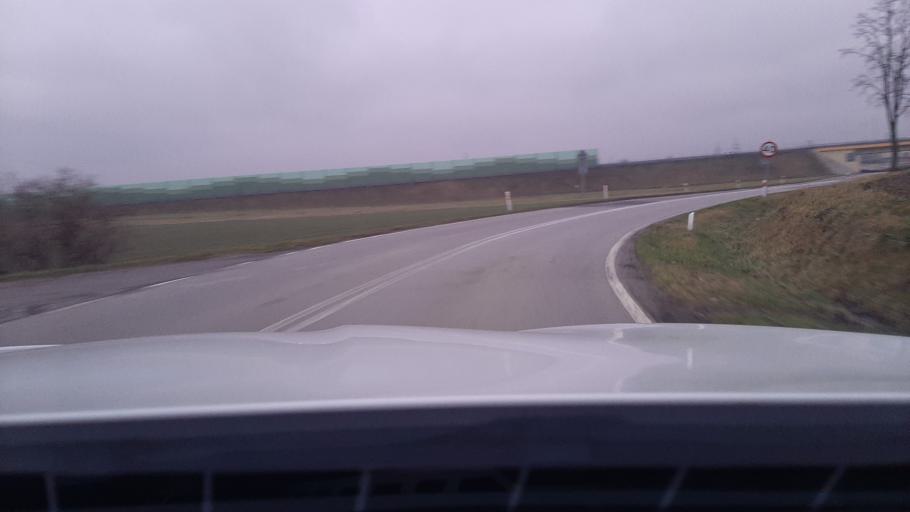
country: PL
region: Lublin Voivodeship
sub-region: Powiat lubelski
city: Garbow
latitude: 51.3487
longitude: 22.3659
